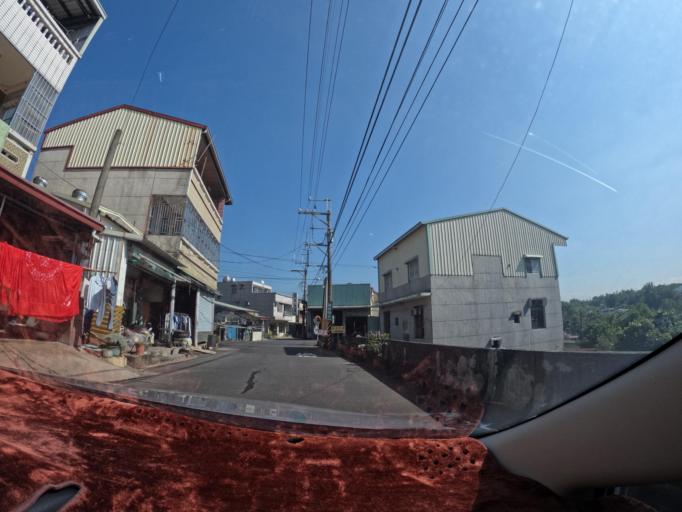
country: TW
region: Taiwan
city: Yujing
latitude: 23.0421
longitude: 120.3627
